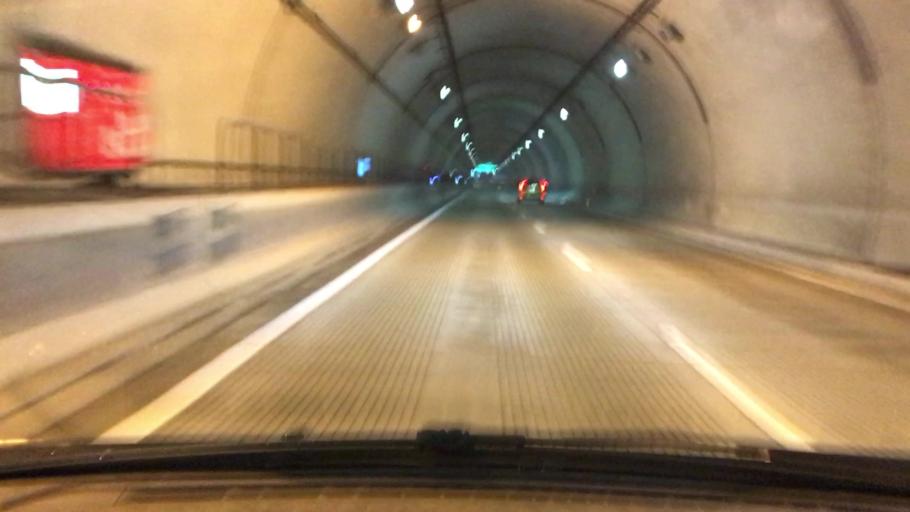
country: JP
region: Hyogo
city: Sandacho
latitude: 34.8254
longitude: 135.2593
